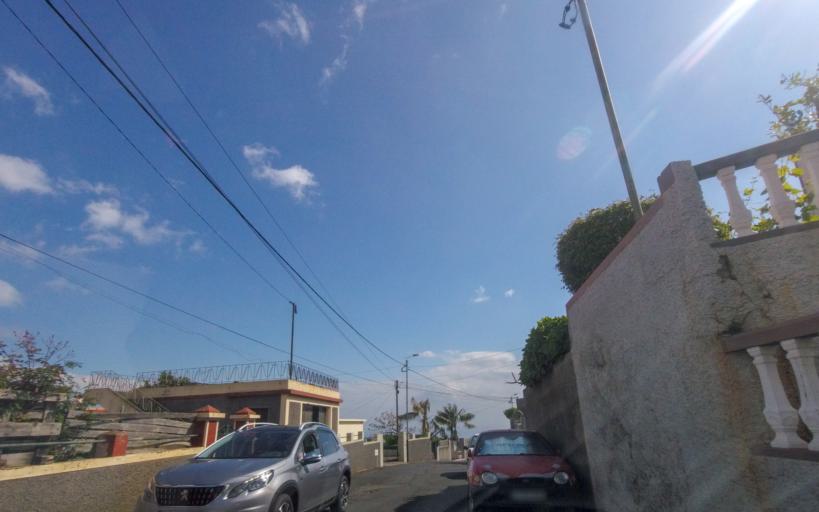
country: PT
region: Madeira
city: Camara de Lobos
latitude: 32.6719
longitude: -16.9475
